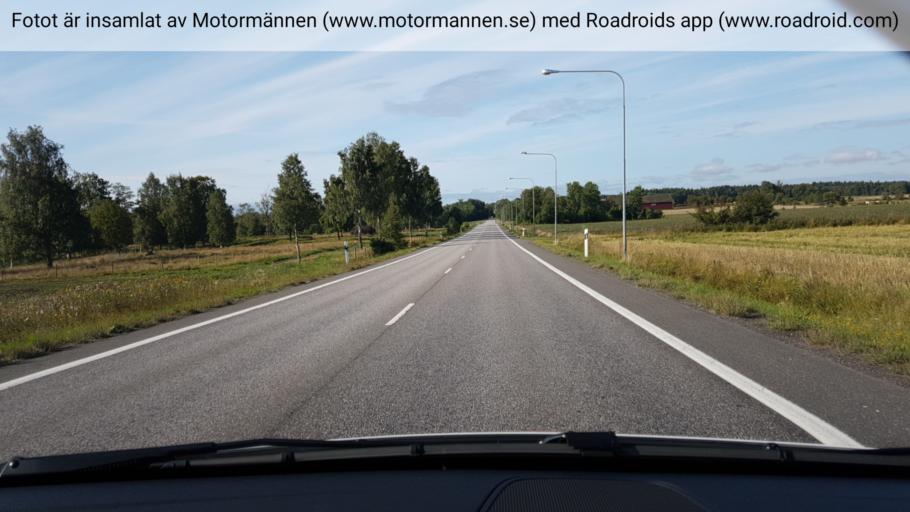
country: SE
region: Vaestra Goetaland
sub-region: Tidaholms Kommun
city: Tidaholm
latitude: 58.1630
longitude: 13.9356
